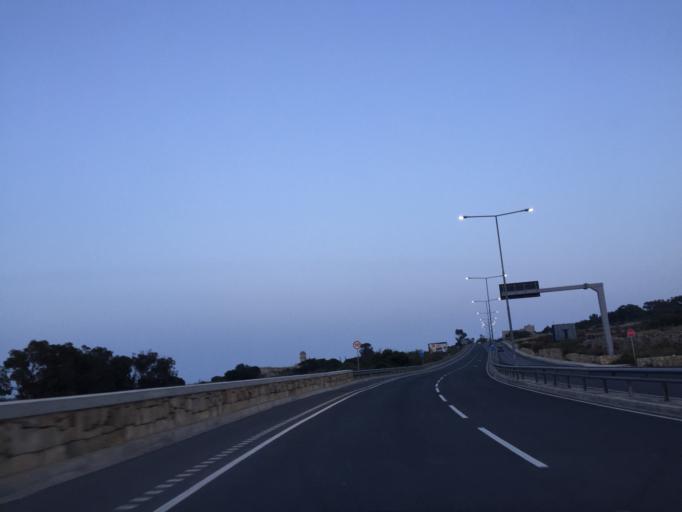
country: MT
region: Pembroke
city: Pembroke
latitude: 35.9326
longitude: 14.4660
